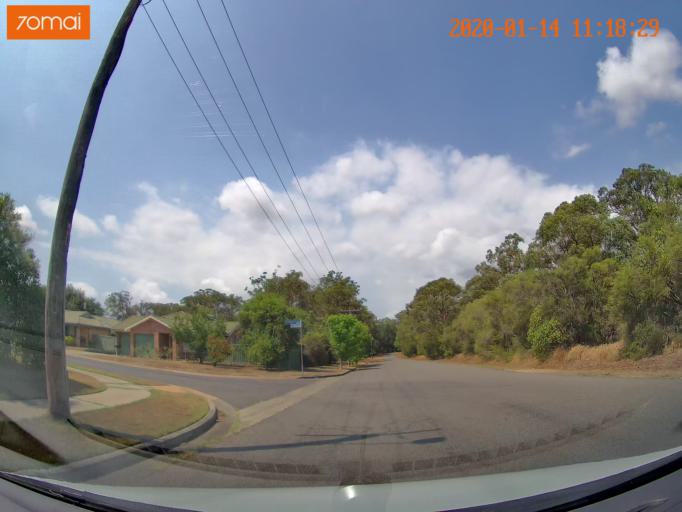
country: AU
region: New South Wales
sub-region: Lake Macquarie Shire
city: Cooranbong
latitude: -33.0974
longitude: 151.4605
